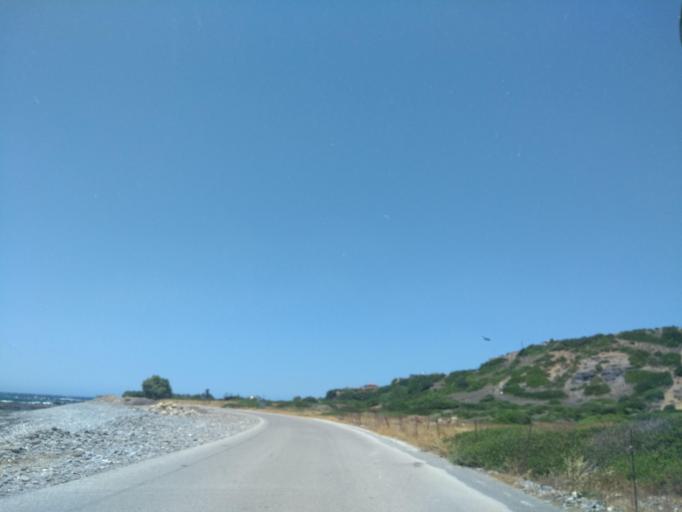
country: GR
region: Crete
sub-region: Nomos Chanias
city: Vryses
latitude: 35.3552
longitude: 23.5331
